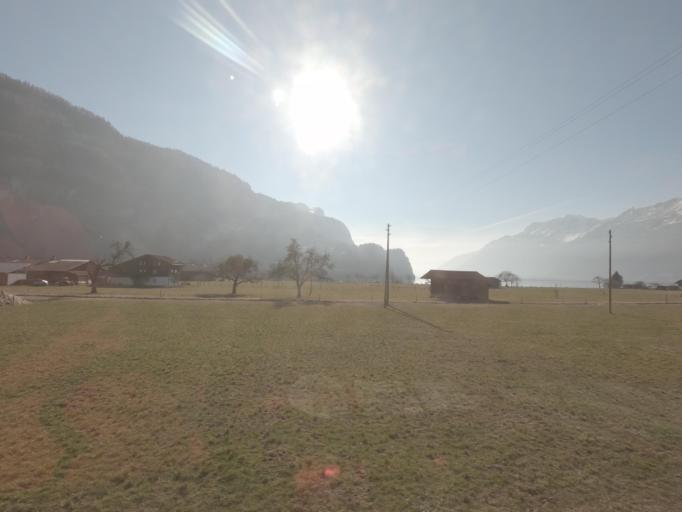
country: CH
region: Bern
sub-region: Interlaken-Oberhasli District
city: Brienz
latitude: 46.7463
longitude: 8.0526
